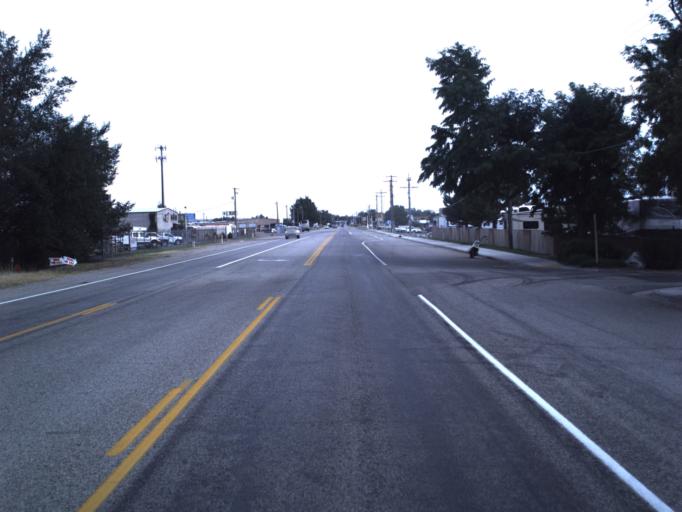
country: US
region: Utah
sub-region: Weber County
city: Farr West
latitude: 41.2789
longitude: -112.0281
